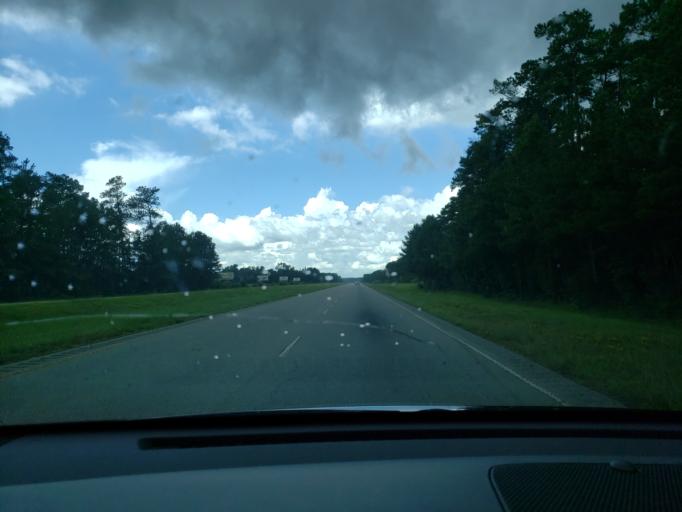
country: US
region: North Carolina
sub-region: Bladen County
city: Elizabethtown
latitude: 34.6171
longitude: -78.6441
